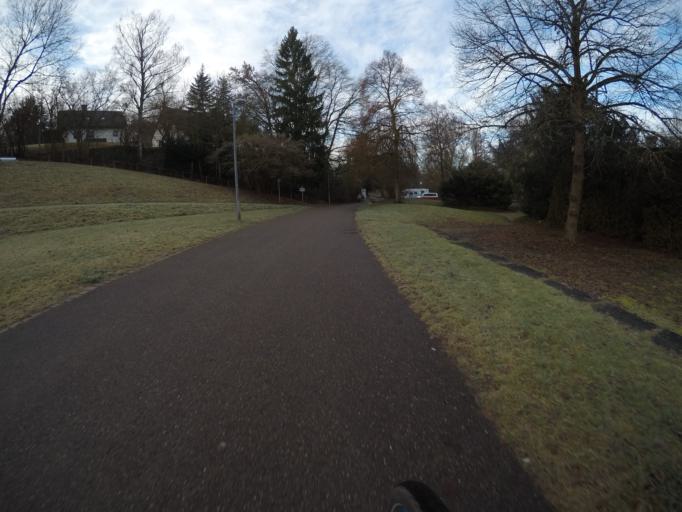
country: DE
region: Baden-Wuerttemberg
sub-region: Regierungsbezirk Stuttgart
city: Sindelfingen
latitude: 48.7144
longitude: 9.0065
